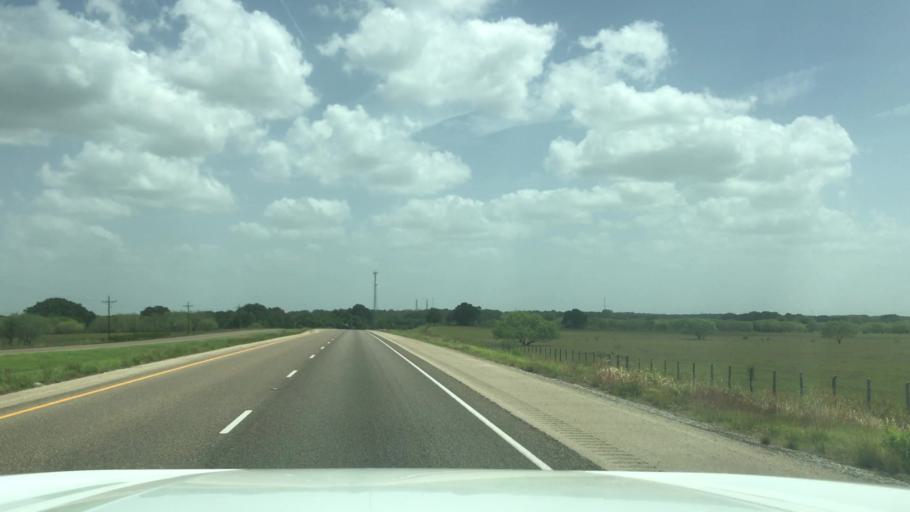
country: US
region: Texas
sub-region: Robertson County
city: Calvert
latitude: 31.1276
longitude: -96.7157
